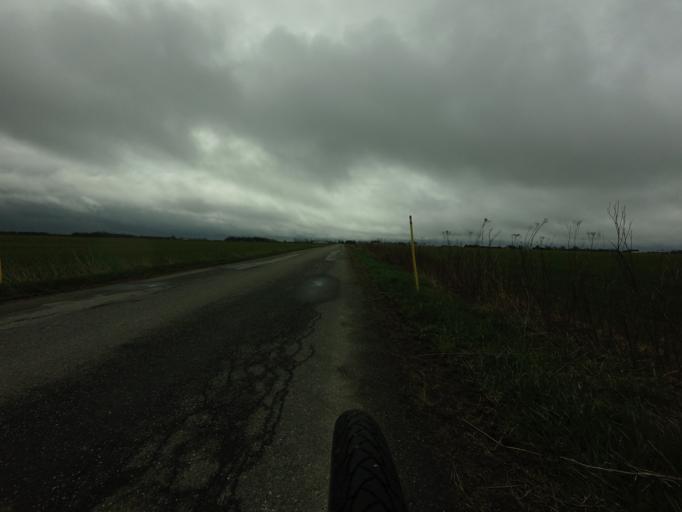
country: DK
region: North Denmark
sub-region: Hjorring Kommune
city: Vra
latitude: 57.3738
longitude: 9.8388
